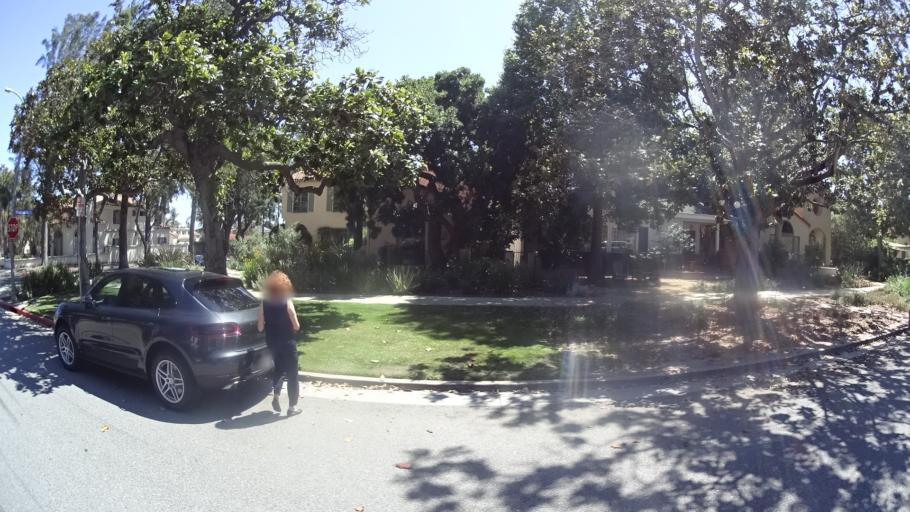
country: US
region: California
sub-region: Los Angeles County
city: Santa Monica
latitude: 34.0374
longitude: -118.4957
